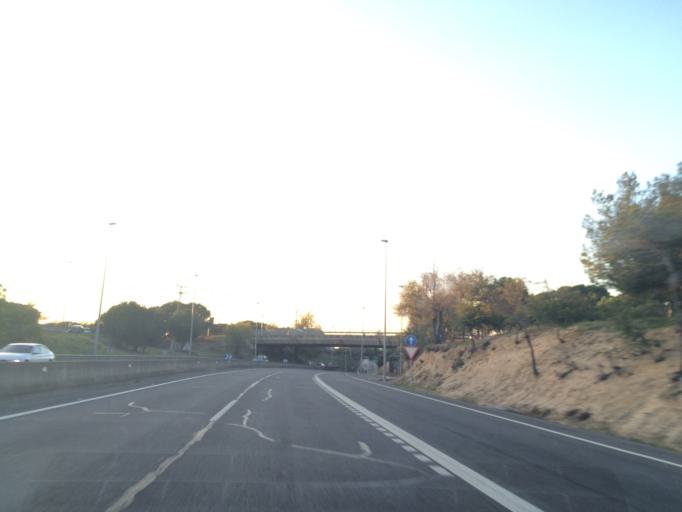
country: ES
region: Madrid
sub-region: Provincia de Madrid
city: Moncloa-Aravaca
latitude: 40.4487
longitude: -3.7611
